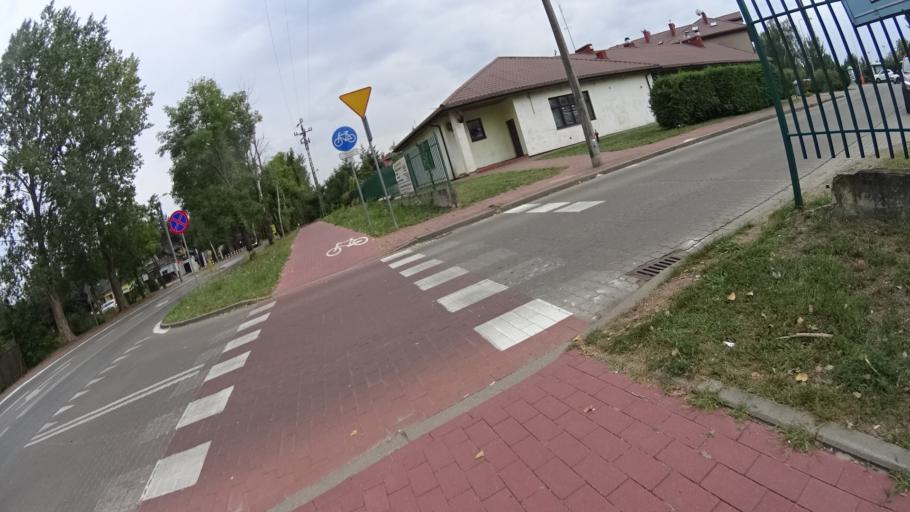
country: PL
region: Masovian Voivodeship
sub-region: Powiat pruszkowski
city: Nadarzyn
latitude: 52.1061
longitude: 20.8019
